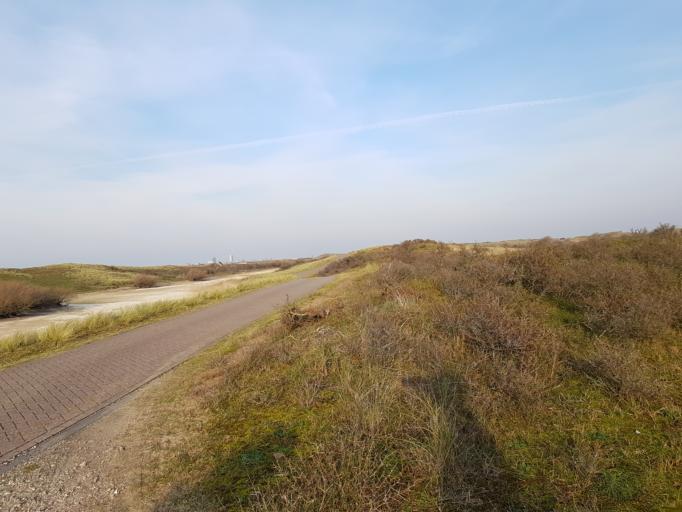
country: NL
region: North Holland
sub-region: Gemeente Zandvoort
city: Zandvoort
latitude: 52.3437
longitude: 4.5204
